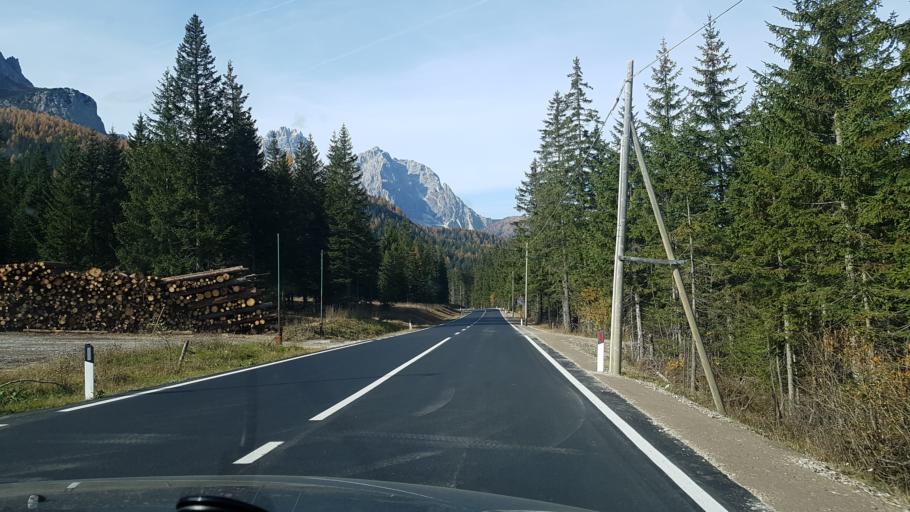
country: IT
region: Trentino-Alto Adige
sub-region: Bolzano
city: Sesto
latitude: 46.6580
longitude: 12.4150
